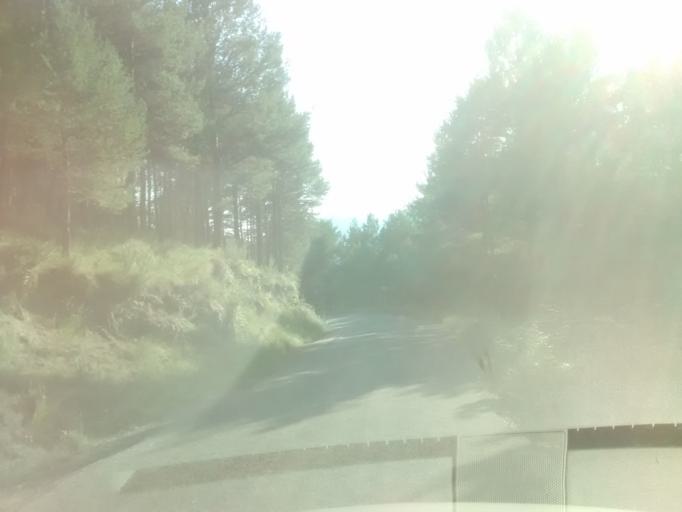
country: ES
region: Aragon
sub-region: Provincia de Huesca
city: Puertolas
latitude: 42.5552
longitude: 0.1692
